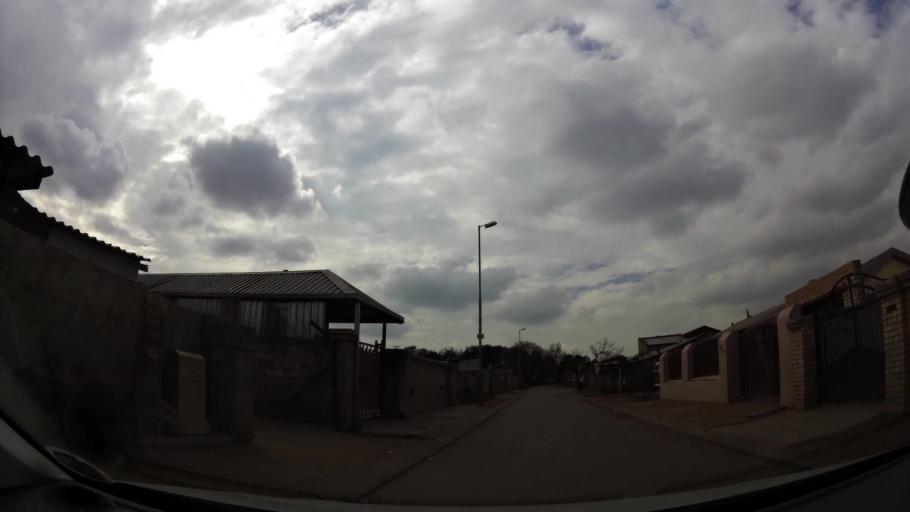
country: ZA
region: Gauteng
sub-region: City of Johannesburg Metropolitan Municipality
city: Soweto
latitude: -26.2717
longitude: 27.8548
